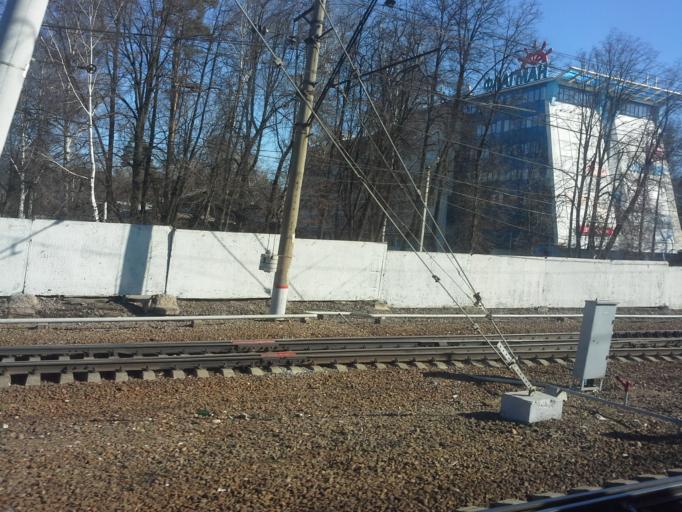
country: RU
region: Moskovskaya
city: Pushkino
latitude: 56.0088
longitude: 37.8376
